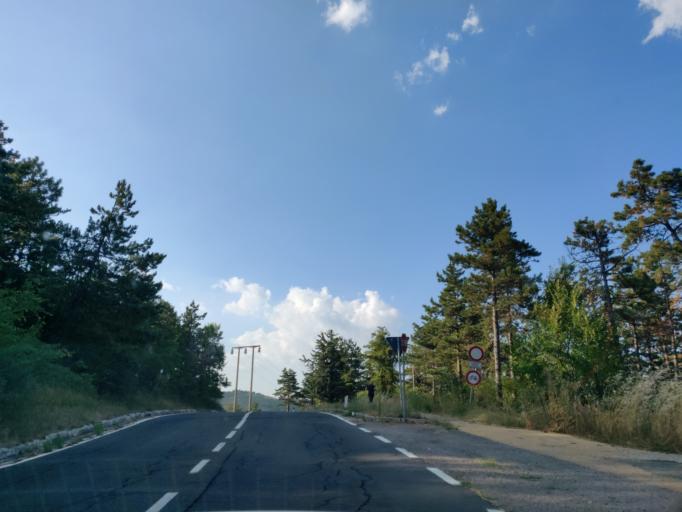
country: IT
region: Tuscany
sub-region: Provincia di Siena
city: Piancastagnaio
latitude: 42.8601
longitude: 11.6824
